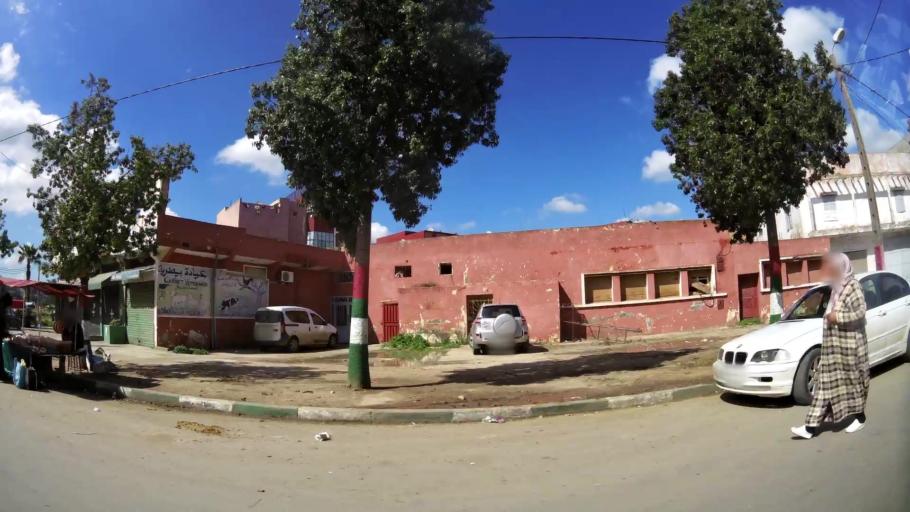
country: MA
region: Grand Casablanca
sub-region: Mediouna
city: Mediouna
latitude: 33.4534
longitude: -7.5152
